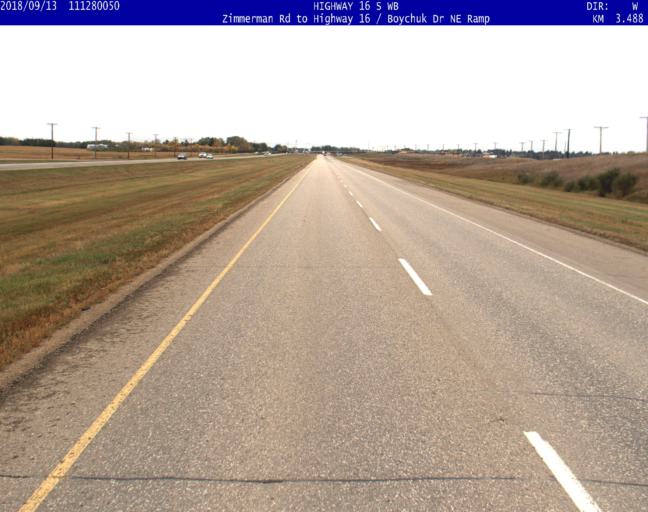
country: CA
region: Saskatchewan
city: Saskatoon
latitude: 52.0862
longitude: -106.5477
